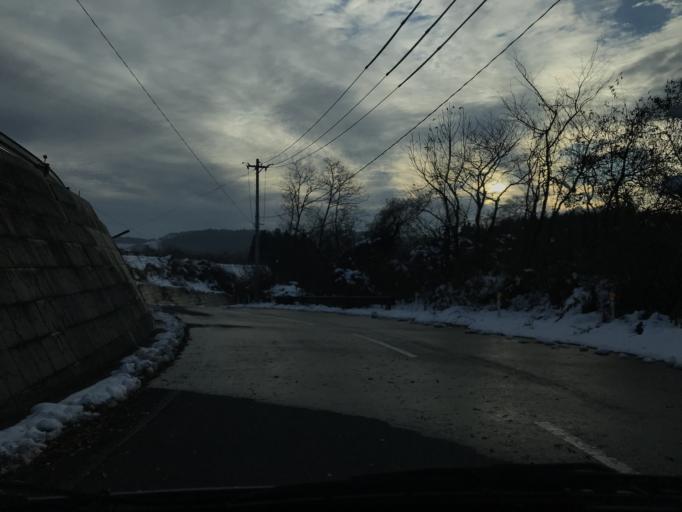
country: JP
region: Iwate
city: Mizusawa
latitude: 39.0591
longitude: 141.0874
